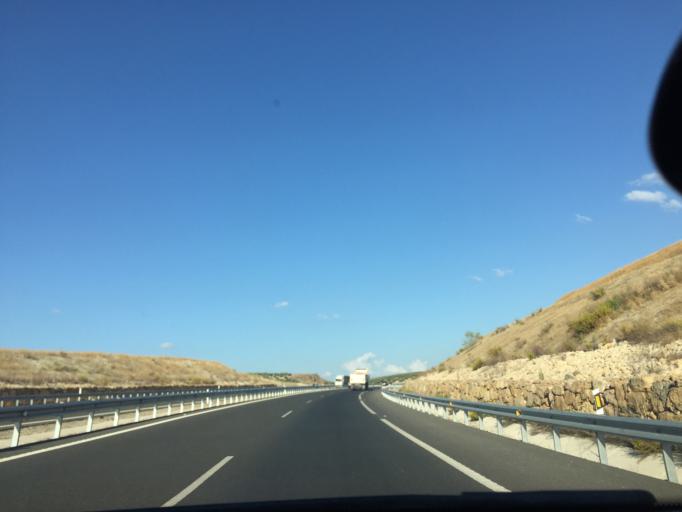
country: ES
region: Andalusia
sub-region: Provincia de Jaen
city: Mancha Real
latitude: 37.8085
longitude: -3.6702
